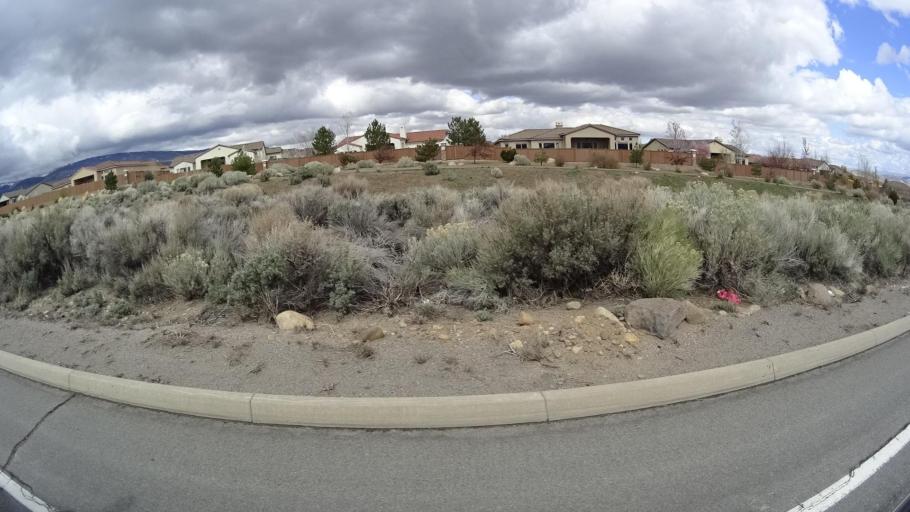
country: US
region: Nevada
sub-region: Washoe County
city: Sparks
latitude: 39.4055
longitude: -119.7653
